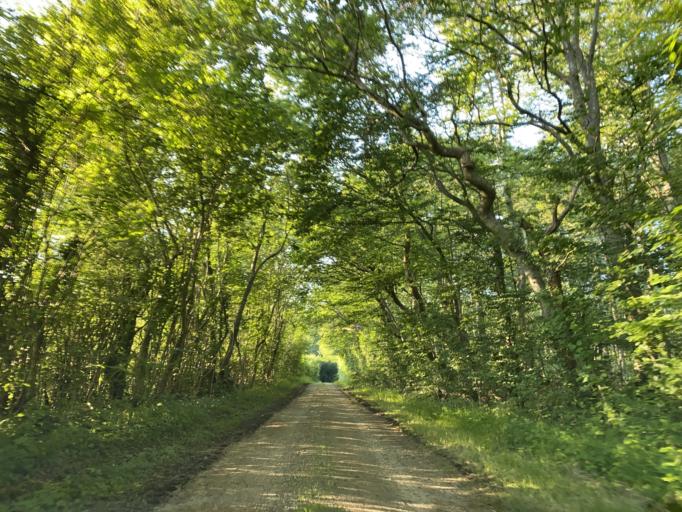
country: DK
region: South Denmark
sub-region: Haderslev Kommune
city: Starup
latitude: 55.1634
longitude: 9.5113
